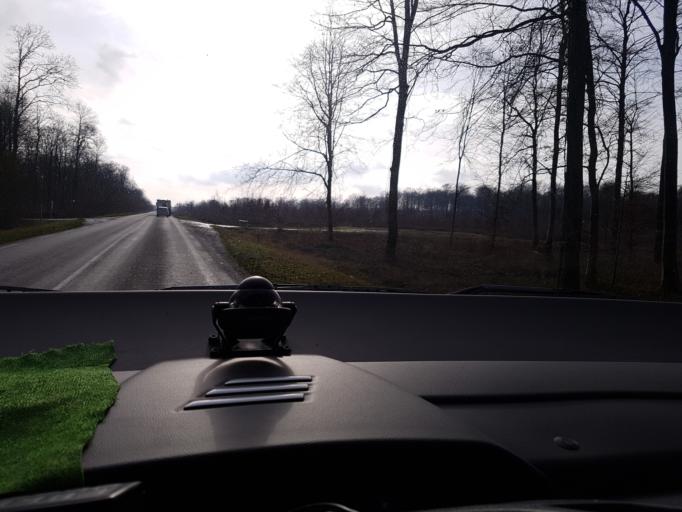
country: FR
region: Nord-Pas-de-Calais
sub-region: Departement du Nord
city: Fourmies
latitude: 49.9929
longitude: 4.0361
